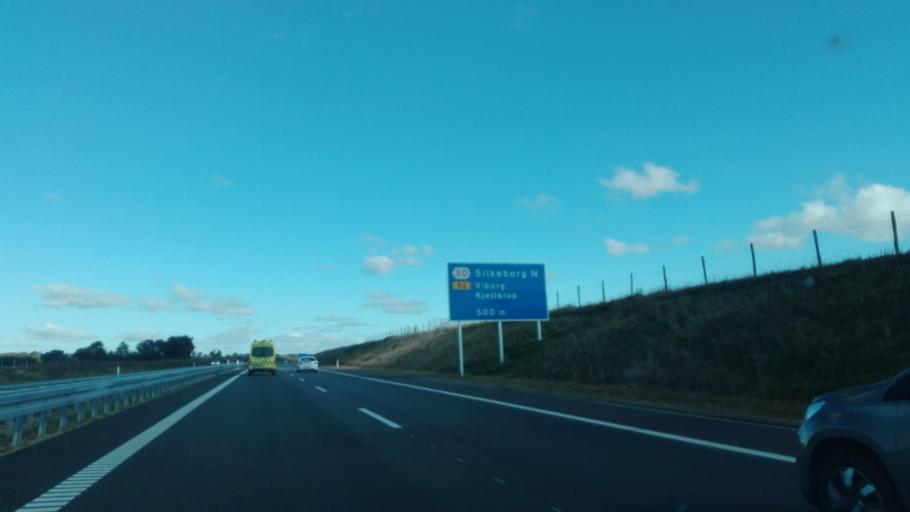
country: DK
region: Central Jutland
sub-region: Silkeborg Kommune
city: Silkeborg
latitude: 56.1934
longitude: 9.5009
